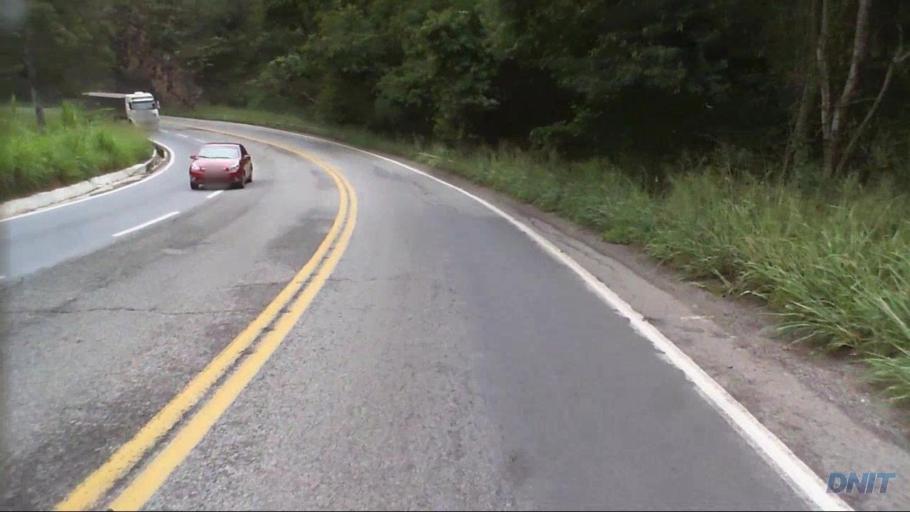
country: BR
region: Minas Gerais
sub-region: Joao Monlevade
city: Joao Monlevade
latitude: -19.8450
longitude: -43.3064
